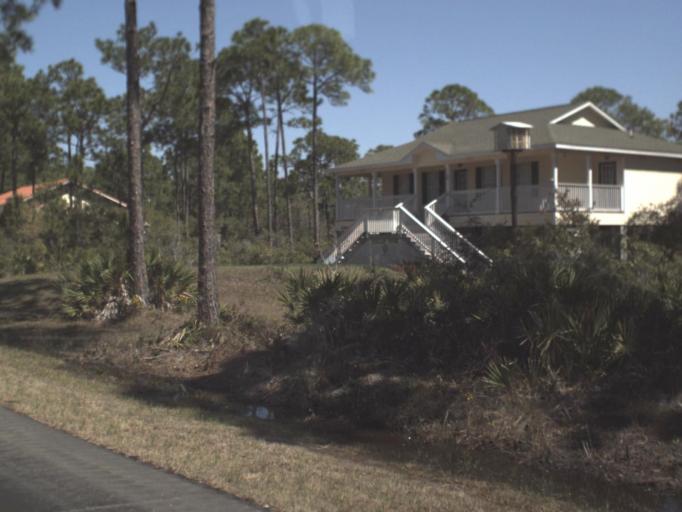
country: US
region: Florida
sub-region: Gulf County
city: Port Saint Joe
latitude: 29.7115
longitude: -85.3033
